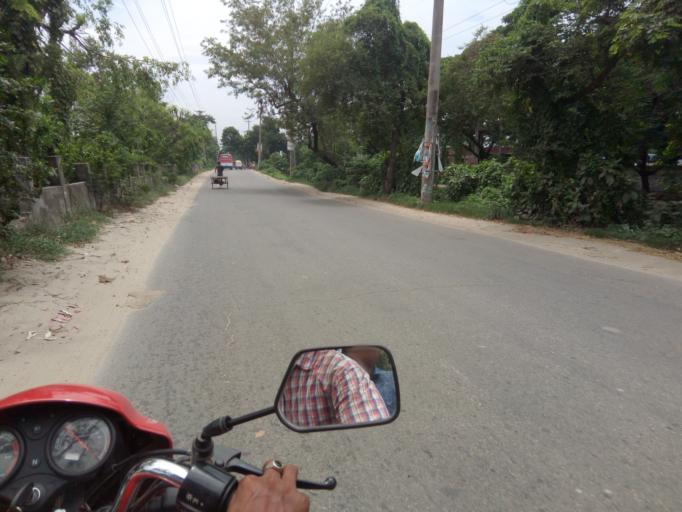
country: BD
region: Dhaka
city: Paltan
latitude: 23.7191
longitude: 90.4876
